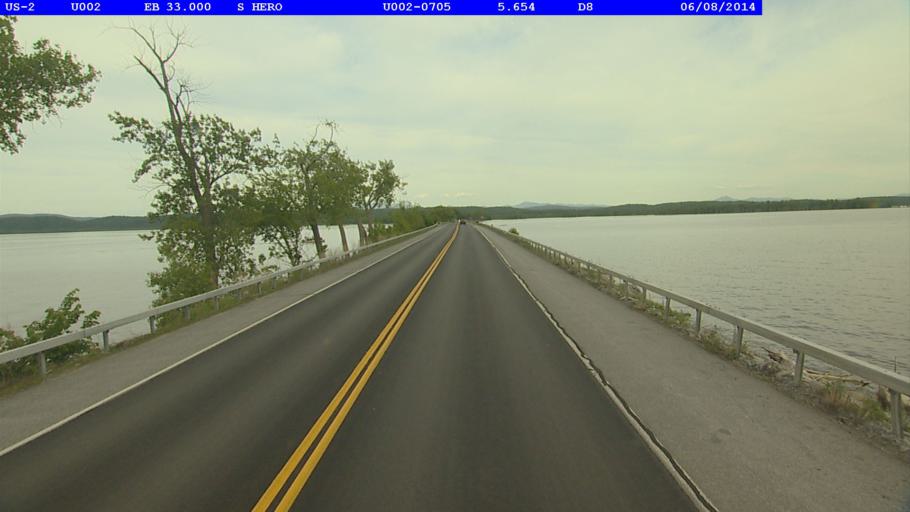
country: US
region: Vermont
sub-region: Chittenden County
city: Colchester
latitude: 44.6323
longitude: -73.2583
